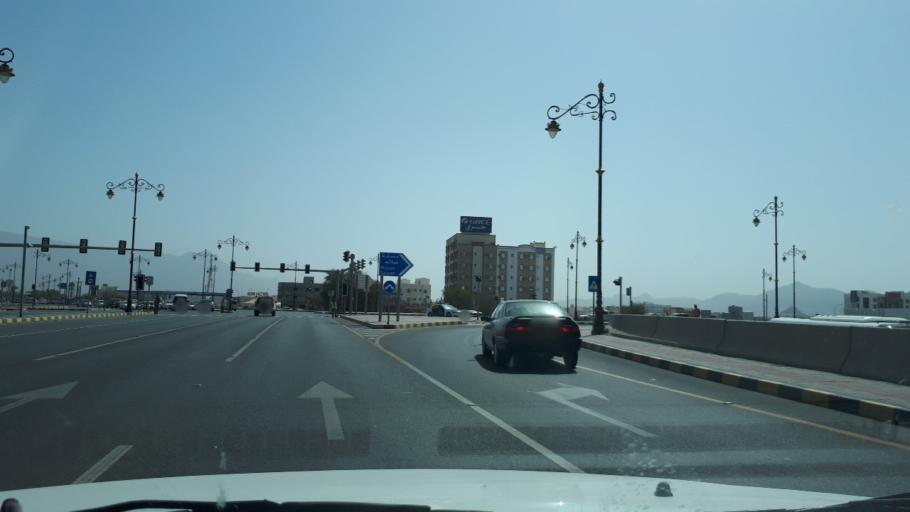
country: OM
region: Muhafazat ad Dakhiliyah
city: Nizwa
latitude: 22.8749
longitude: 57.5323
